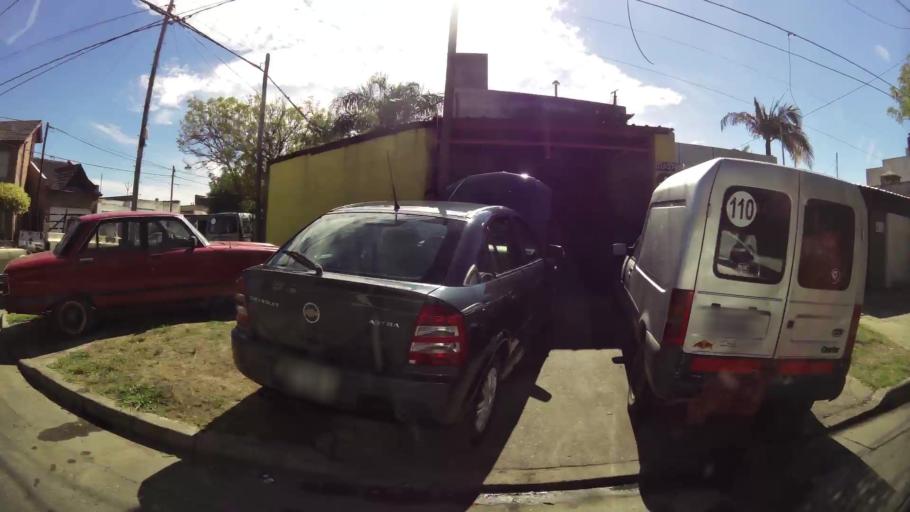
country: AR
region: Santa Fe
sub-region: Departamento de Rosario
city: Rosario
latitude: -32.9357
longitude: -60.7153
